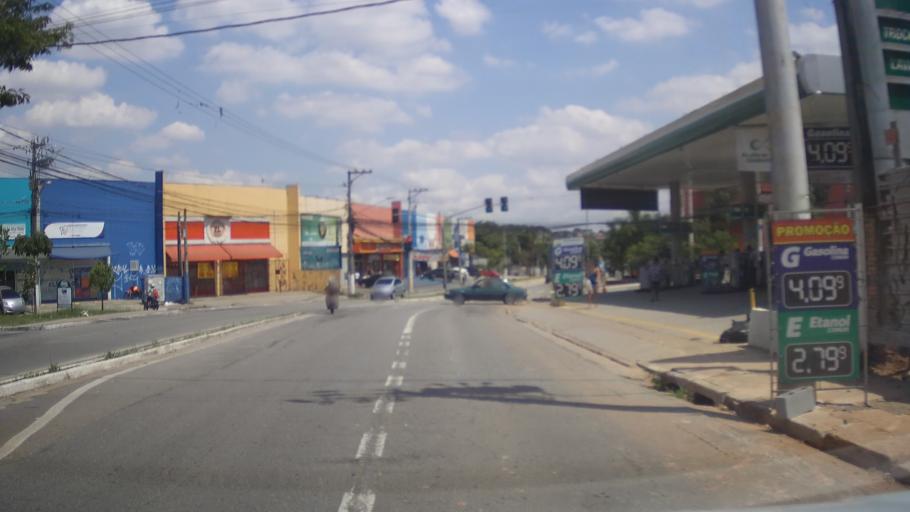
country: BR
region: Sao Paulo
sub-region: Guarulhos
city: Guarulhos
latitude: -23.4265
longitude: -46.5225
